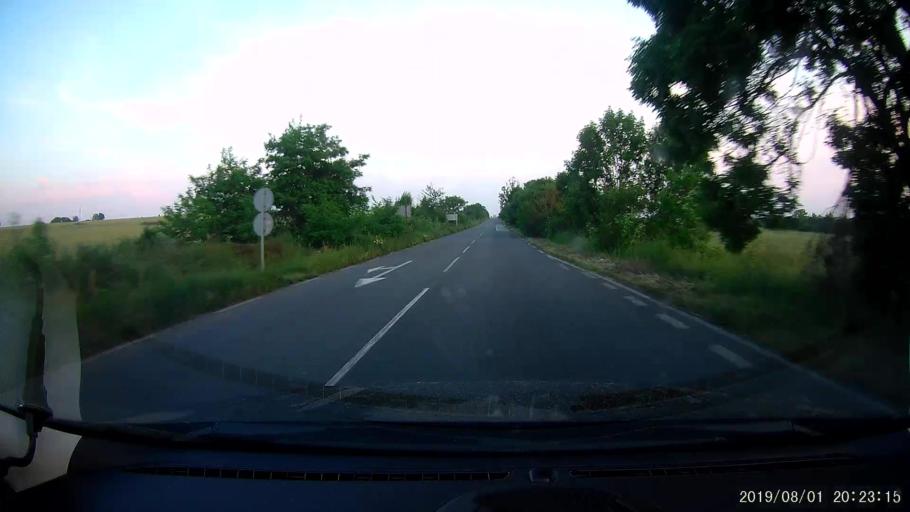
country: BG
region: Yambol
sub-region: Obshtina Elkhovo
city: Elkhovo
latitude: 42.2524
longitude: 26.5988
